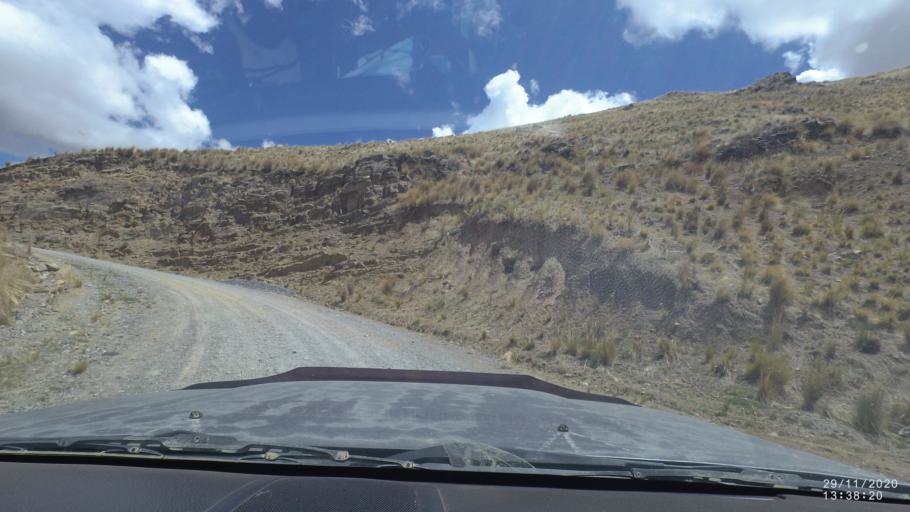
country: BO
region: Cochabamba
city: Cochabamba
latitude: -17.1220
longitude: -66.3294
